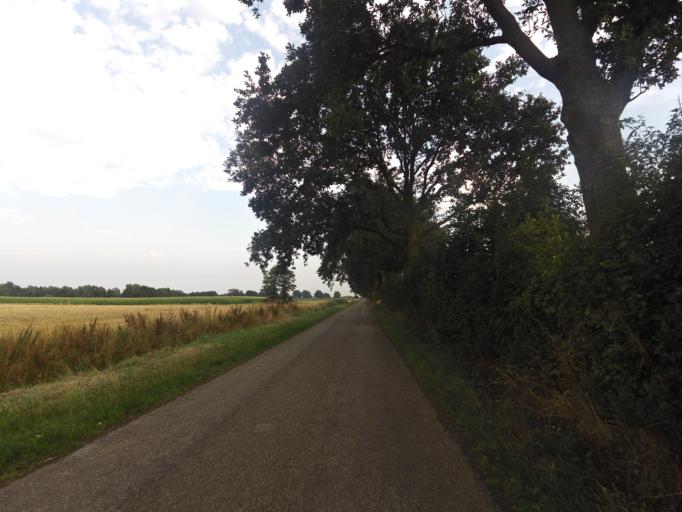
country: NL
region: Gelderland
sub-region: Oude IJsselstreek
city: Gendringen
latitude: 51.9000
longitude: 6.3385
